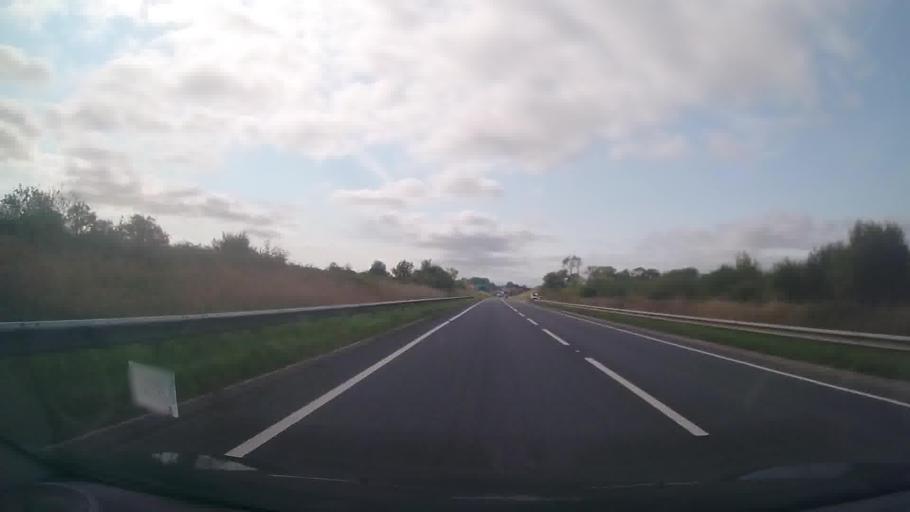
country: GB
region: Wales
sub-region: Pembrokeshire
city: Jeffreyston
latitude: 51.6949
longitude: -4.8027
